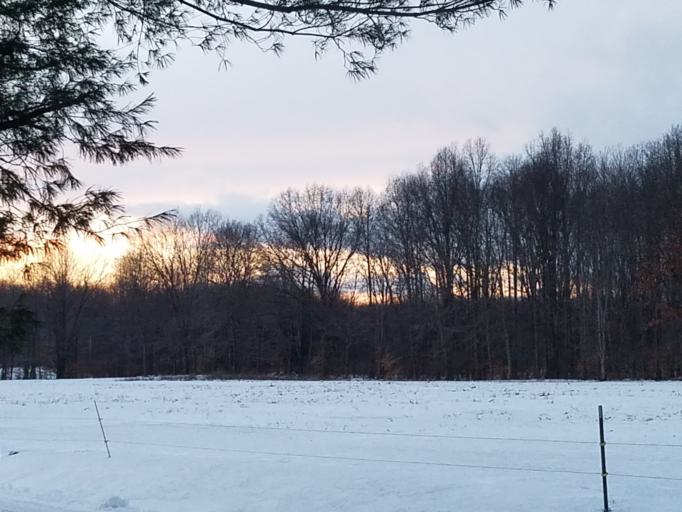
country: US
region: Pennsylvania
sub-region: Mercer County
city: Mercer
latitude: 41.3426
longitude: -80.2223
